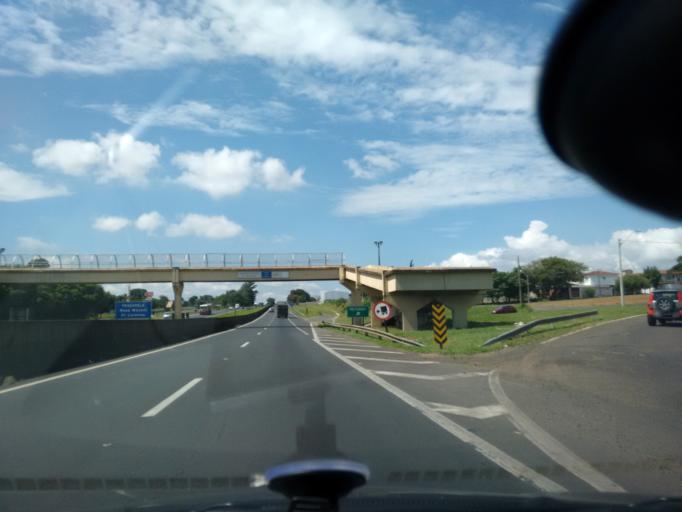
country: BR
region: Sao Paulo
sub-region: Sao Carlos
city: Sao Carlos
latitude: -21.9957
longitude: -47.8774
